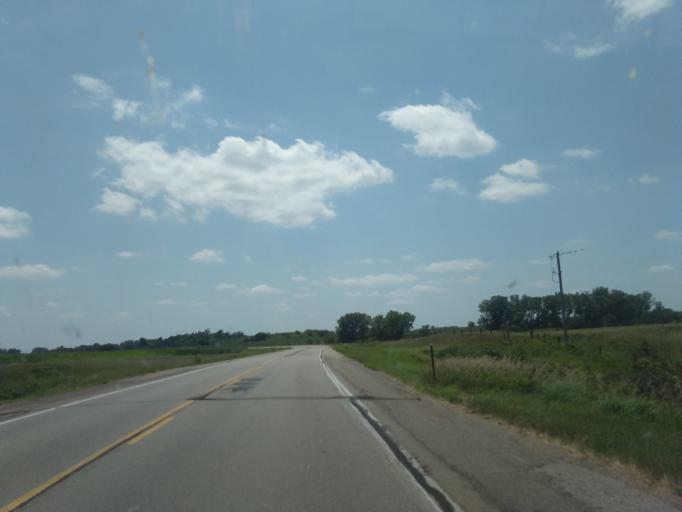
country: US
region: Nebraska
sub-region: Dawson County
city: Lexington
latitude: 40.6996
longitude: -99.7907
